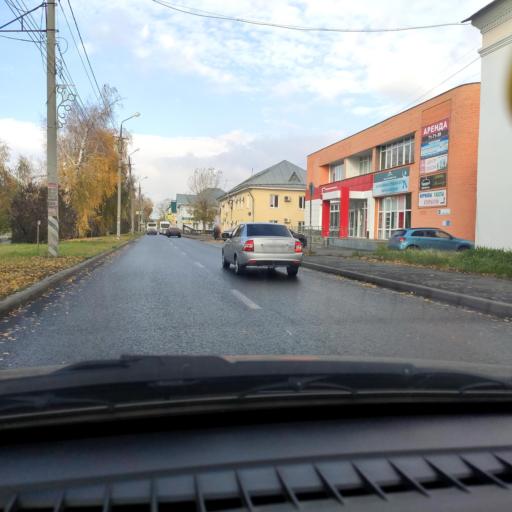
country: RU
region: Samara
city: Tol'yatti
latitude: 53.5148
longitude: 49.4096
